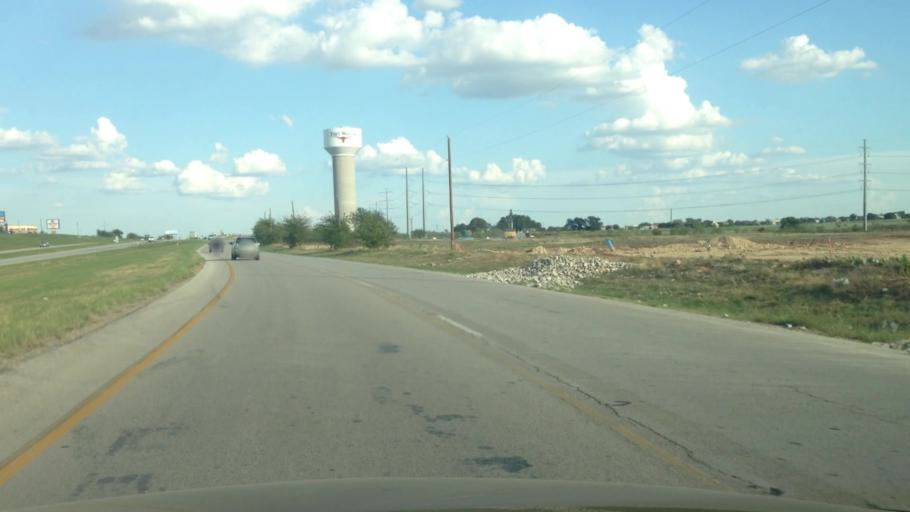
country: US
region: Texas
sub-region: Tarrant County
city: Pecan Acres
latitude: 32.9674
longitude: -97.4188
